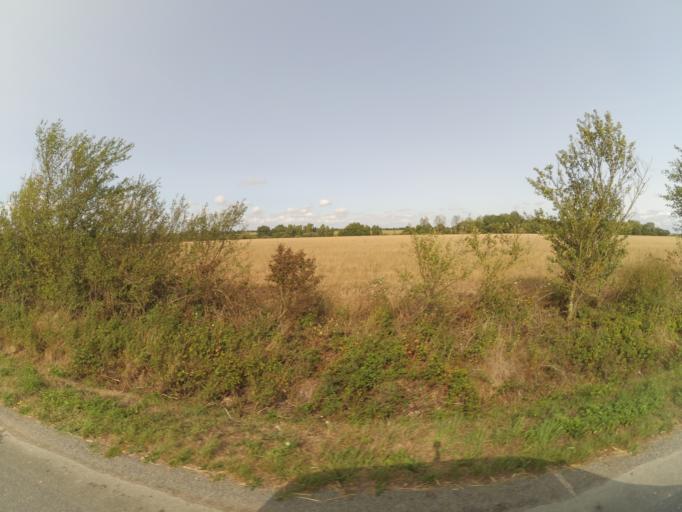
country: FR
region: Pays de la Loire
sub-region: Departement de la Vendee
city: La Bruffiere
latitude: 46.9926
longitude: -1.1902
